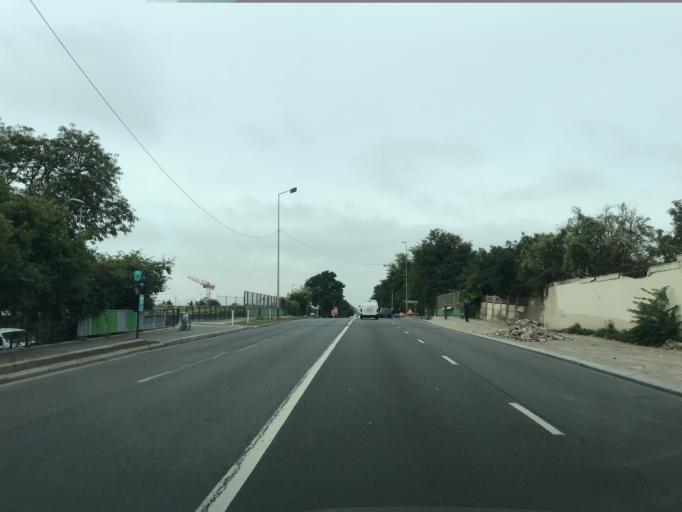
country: FR
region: Ile-de-France
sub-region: Departement de Seine-Saint-Denis
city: Drancy
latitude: 48.9106
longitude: 2.4320
